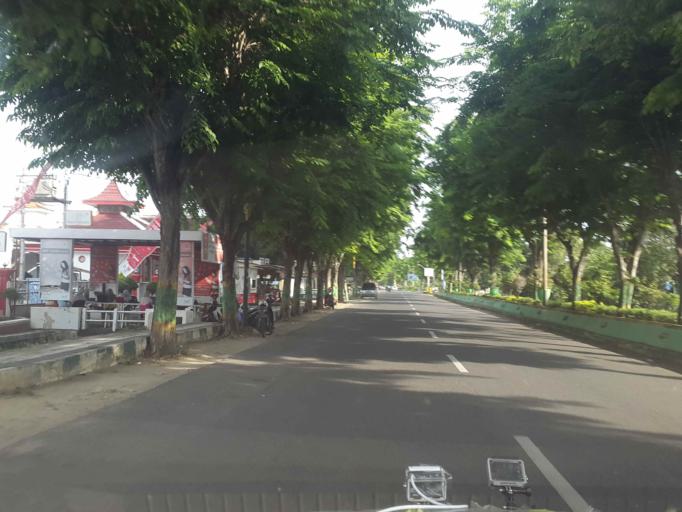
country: ID
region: East Java
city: Sumenep
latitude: -7.0186
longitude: 113.8747
